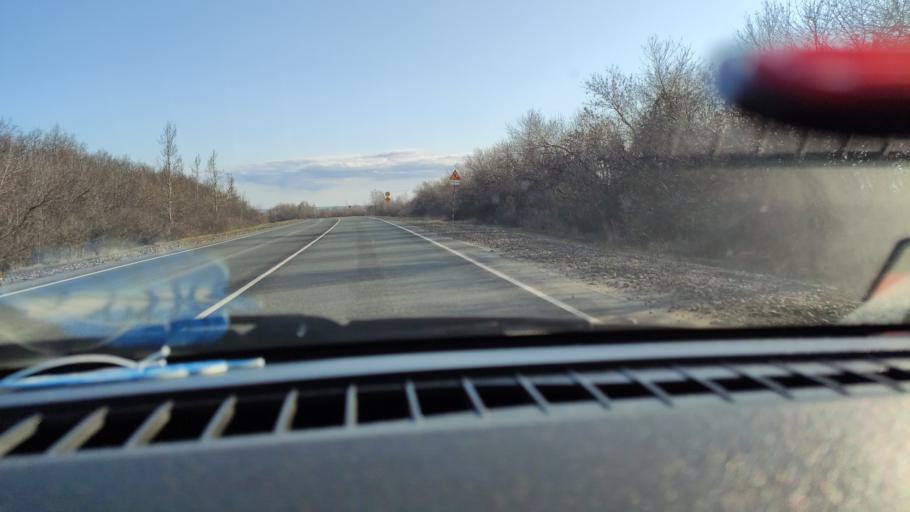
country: RU
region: Saratov
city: Dukhovnitskoye
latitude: 52.6252
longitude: 48.1790
